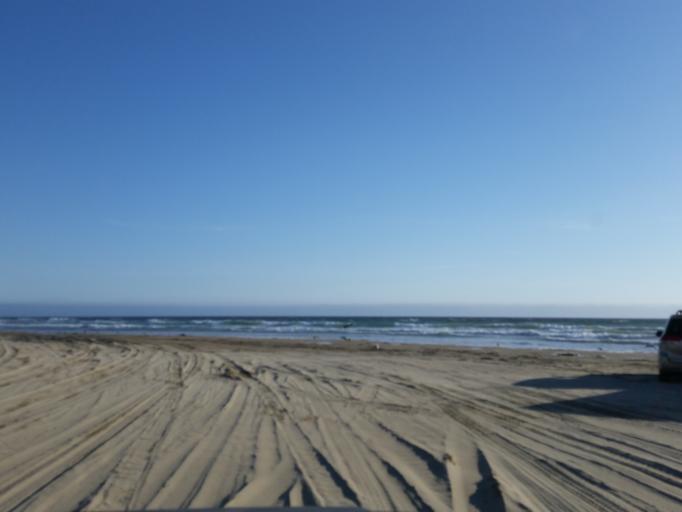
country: US
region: California
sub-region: San Luis Obispo County
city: Grover Beach
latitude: 35.1210
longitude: -120.6354
